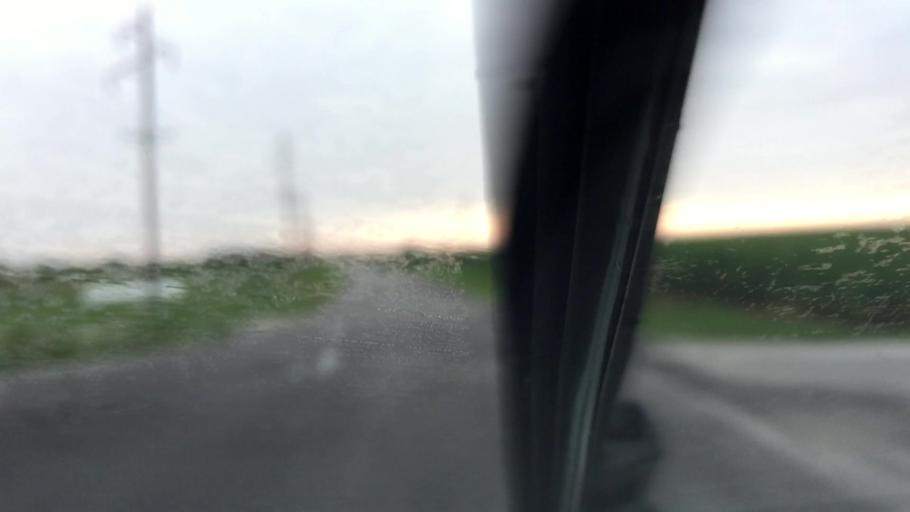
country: US
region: Iowa
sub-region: Lee County
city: Fort Madison
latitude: 40.5507
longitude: -91.2689
